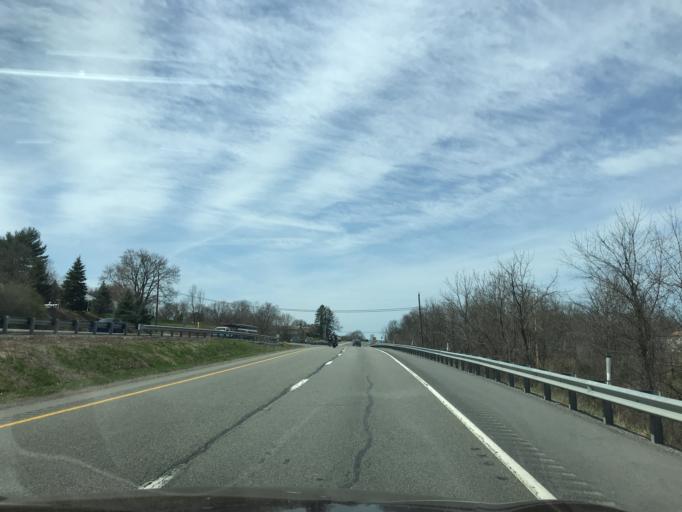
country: US
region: Pennsylvania
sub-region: Union County
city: Lewisburg
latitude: 40.9331
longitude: -76.8710
